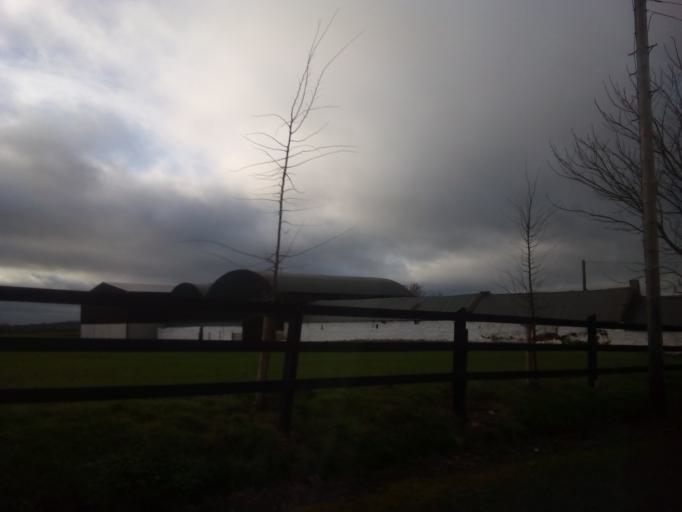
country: IE
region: Leinster
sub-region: Fingal County
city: Skerries
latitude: 53.5555
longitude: -6.1307
